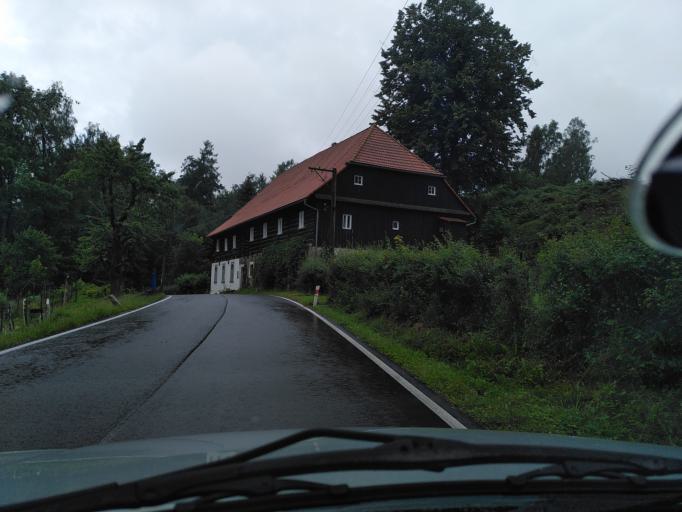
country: CZ
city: Novy Bor
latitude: 50.8071
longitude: 14.5401
